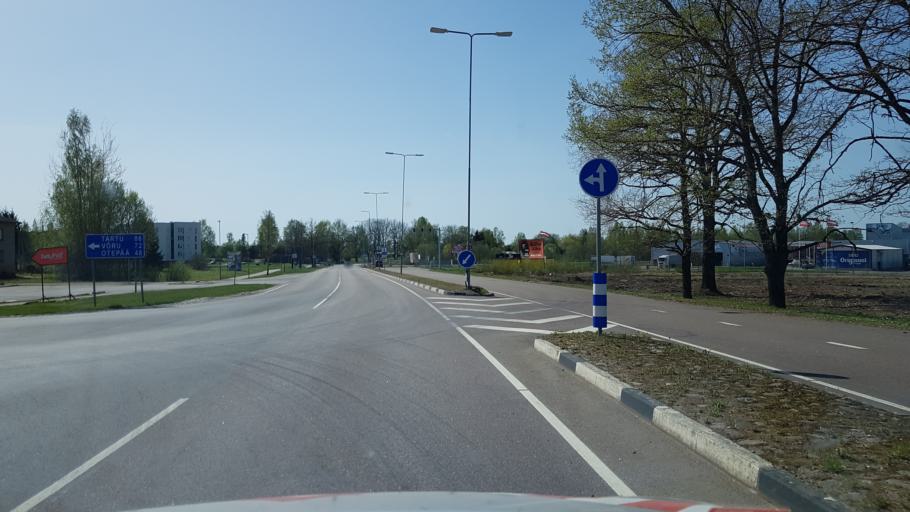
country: EE
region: Valgamaa
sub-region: Valga linn
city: Valga
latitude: 57.7924
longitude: 26.0334
